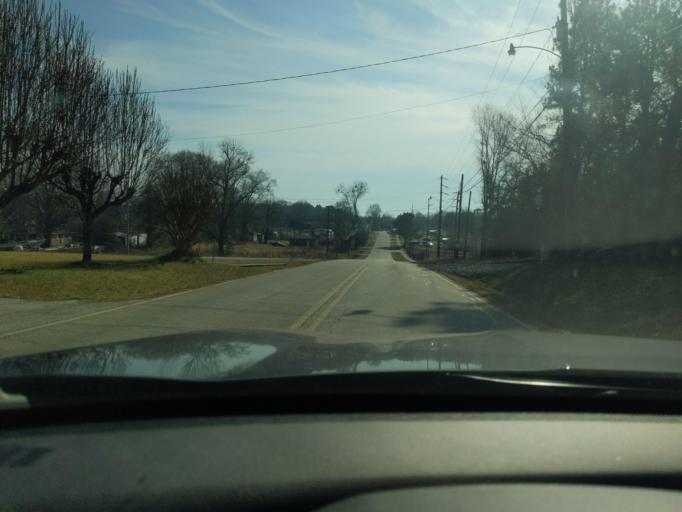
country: US
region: South Carolina
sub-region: Abbeville County
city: Calhoun Falls
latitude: 34.0887
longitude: -82.5899
